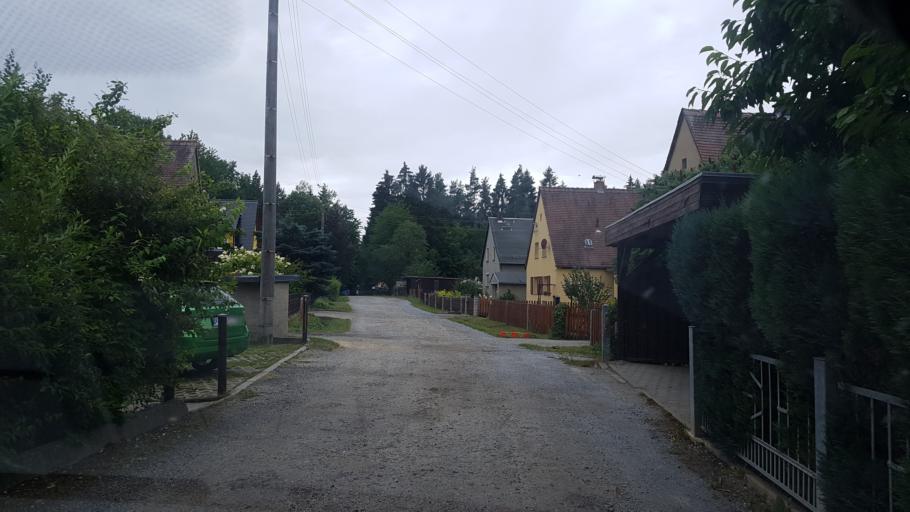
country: DE
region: Saxony
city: Ohorn
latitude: 51.1704
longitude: 14.0434
